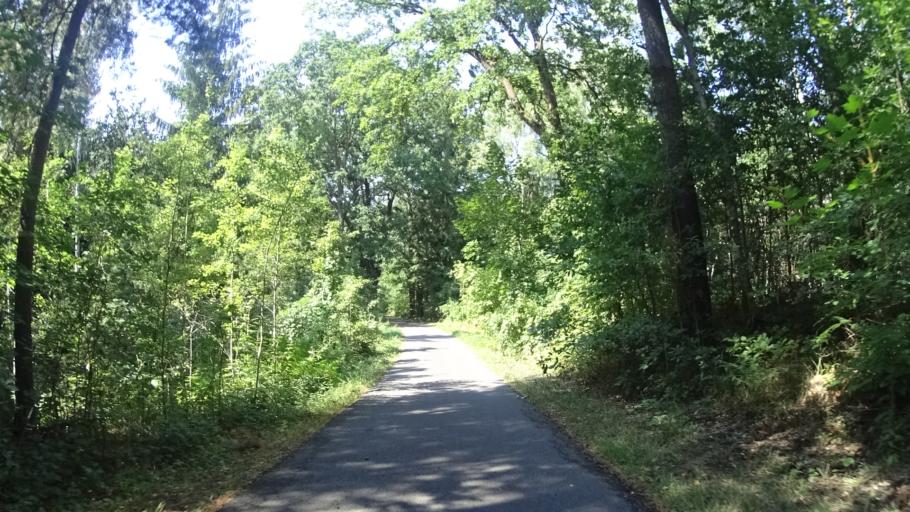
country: DE
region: Saxony
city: Gross Duben
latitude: 51.6035
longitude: 14.5626
